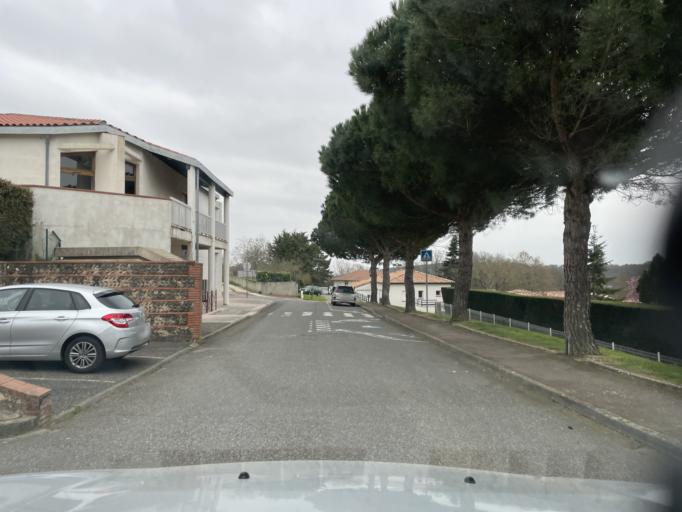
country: FR
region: Midi-Pyrenees
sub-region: Departement du Gers
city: Pujaudran
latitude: 43.5900
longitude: 1.1500
